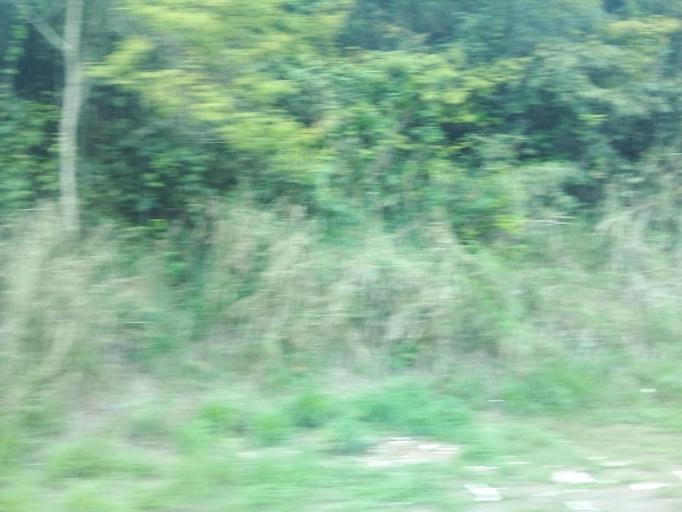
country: BR
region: Minas Gerais
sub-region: Joao Monlevade
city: Joao Monlevade
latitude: -19.8084
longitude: -43.1040
